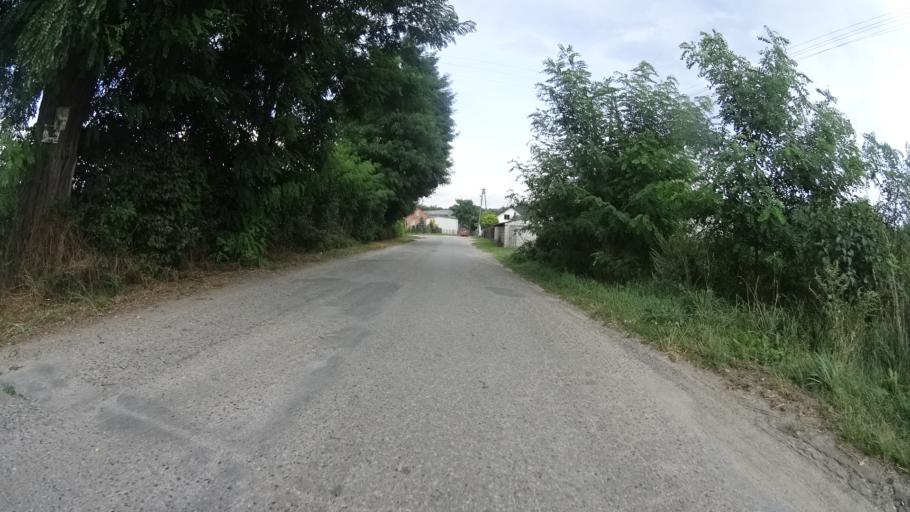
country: PL
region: Masovian Voivodeship
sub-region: Powiat grojecki
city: Mogielnica
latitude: 51.6686
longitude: 20.7397
